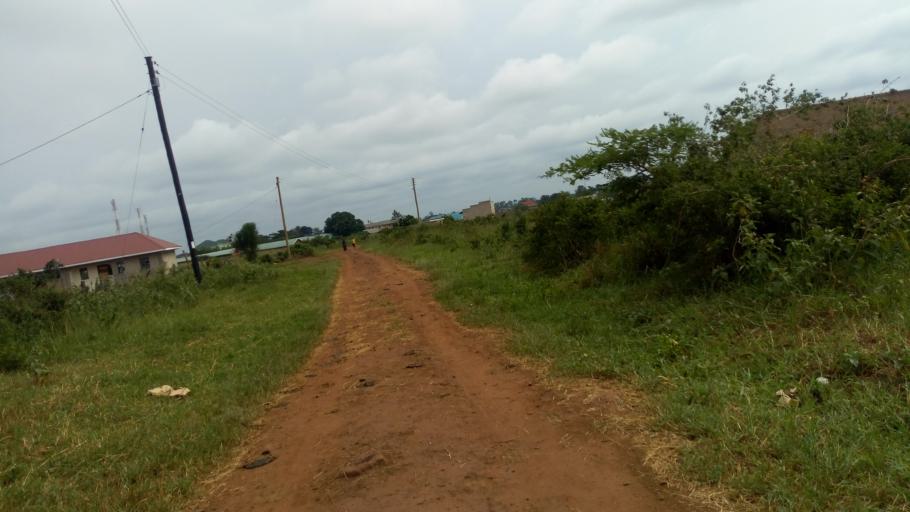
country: UG
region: Western Region
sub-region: Kiryandongo District
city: Kiryandongo
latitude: 1.8029
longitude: 32.0133
